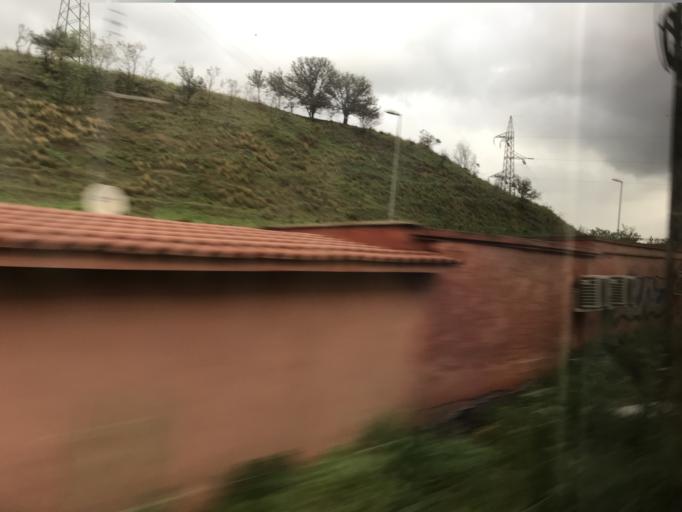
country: IT
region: Latium
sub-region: Citta metropolitana di Roma Capitale
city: Vitinia
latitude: 41.8340
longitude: 12.4391
